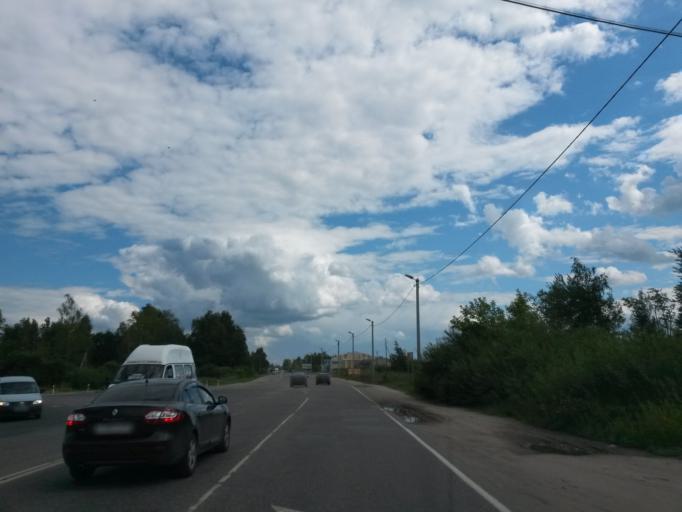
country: RU
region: Ivanovo
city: Novo-Talitsy
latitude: 57.0057
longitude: 40.8740
